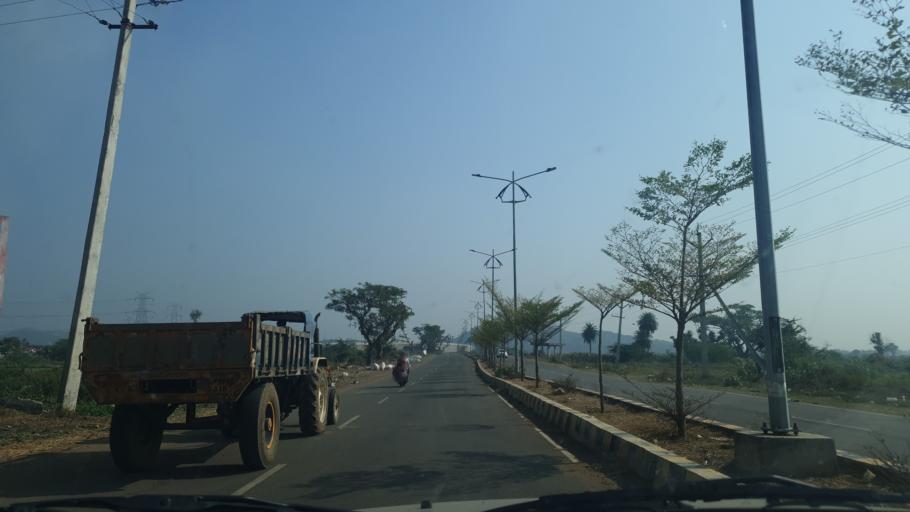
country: IN
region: Andhra Pradesh
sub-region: Srikakulam
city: Tekkali
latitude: 18.6153
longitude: 84.2385
